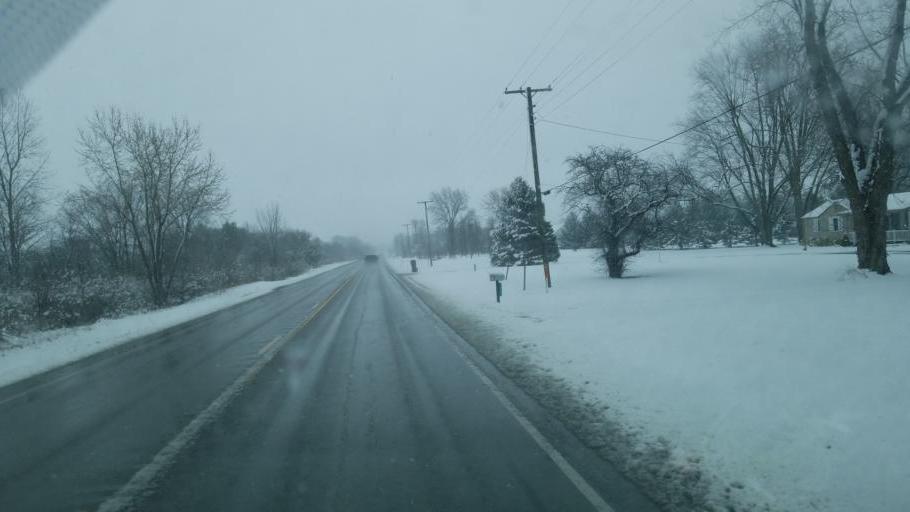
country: US
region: Indiana
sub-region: Delaware County
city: Muncie
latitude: 40.1400
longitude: -85.3379
